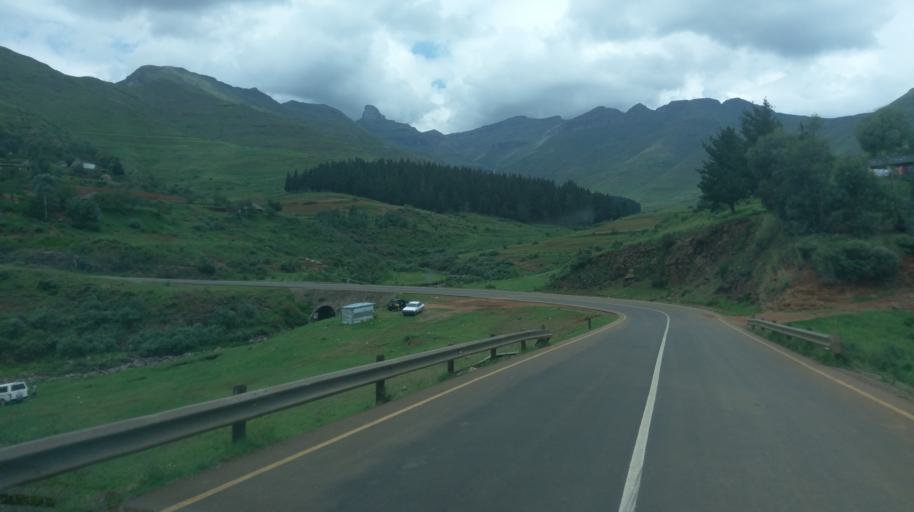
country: LS
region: Butha-Buthe
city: Butha-Buthe
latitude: -29.0367
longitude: 28.2783
